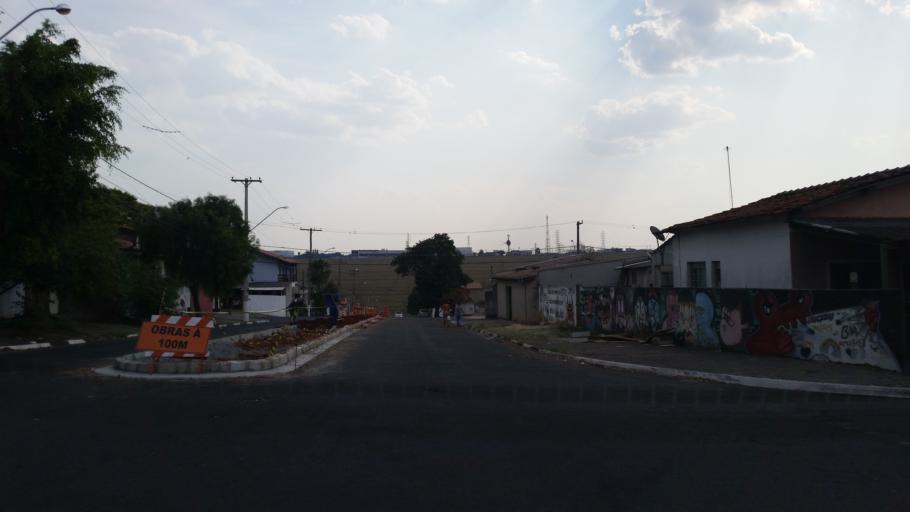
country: BR
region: Sao Paulo
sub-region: Hortolandia
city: Hortolandia
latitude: -22.8896
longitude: -47.1809
